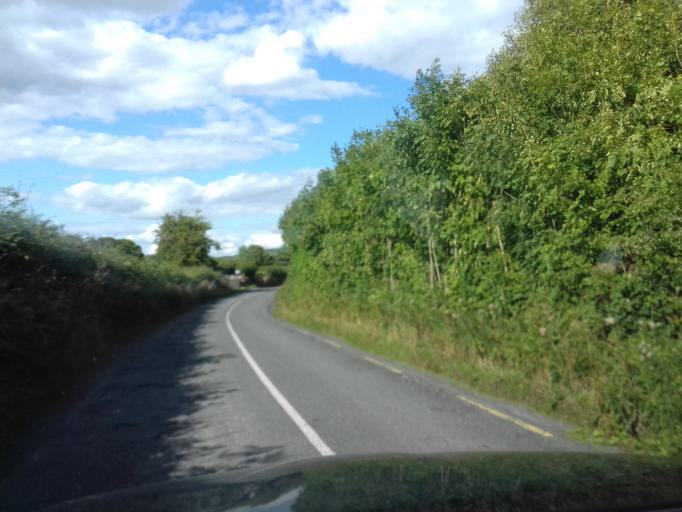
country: IE
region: Leinster
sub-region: Kilkenny
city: Thomastown
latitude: 52.5452
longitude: -7.0842
